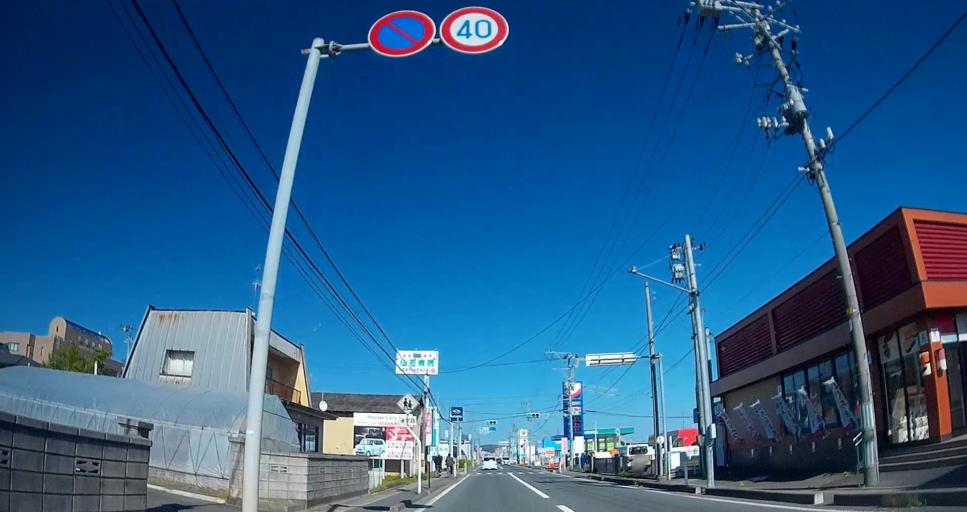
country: JP
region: Miyagi
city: Yamoto
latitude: 38.4309
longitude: 141.2572
